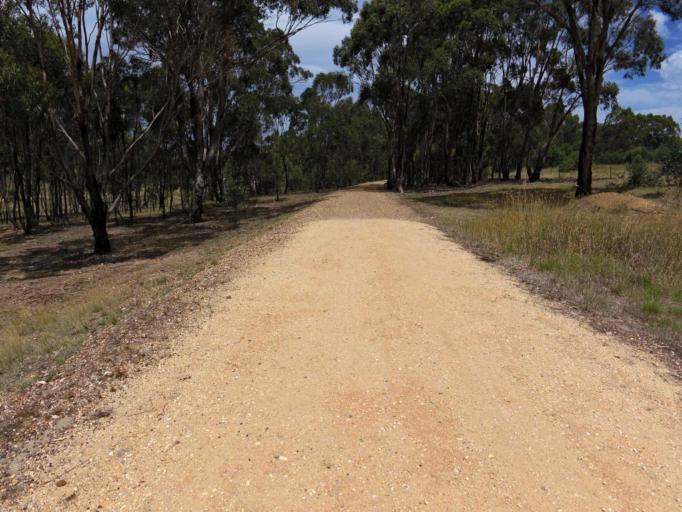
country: AU
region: Victoria
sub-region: Greater Bendigo
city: Kennington
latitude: -36.8831
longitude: 144.6539
